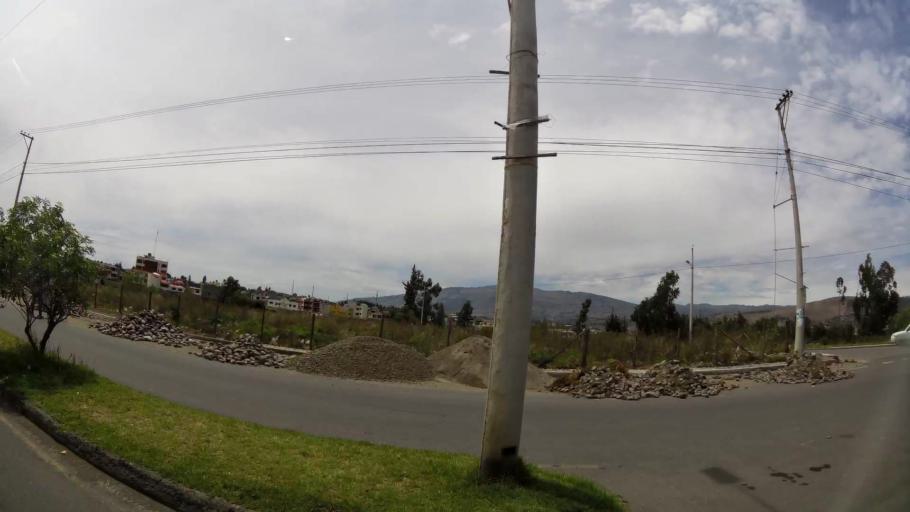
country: EC
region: Cotopaxi
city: San Miguel de Salcedo
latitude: -1.0391
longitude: -78.5865
